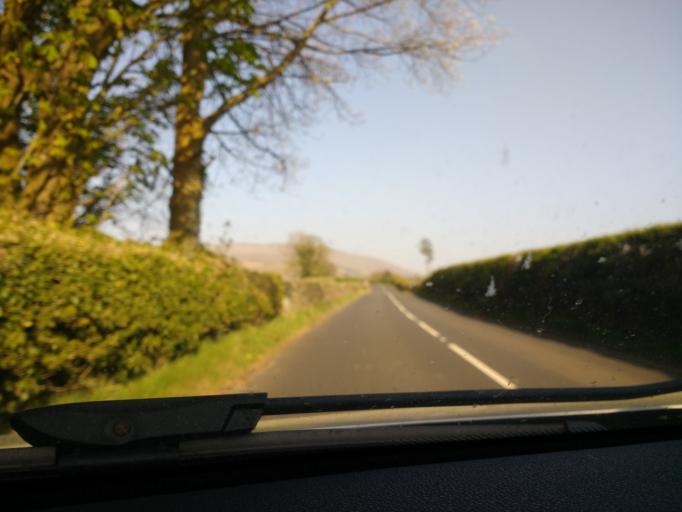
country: GB
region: England
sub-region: Cumbria
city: Sedbergh
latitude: 54.3201
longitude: -2.4980
